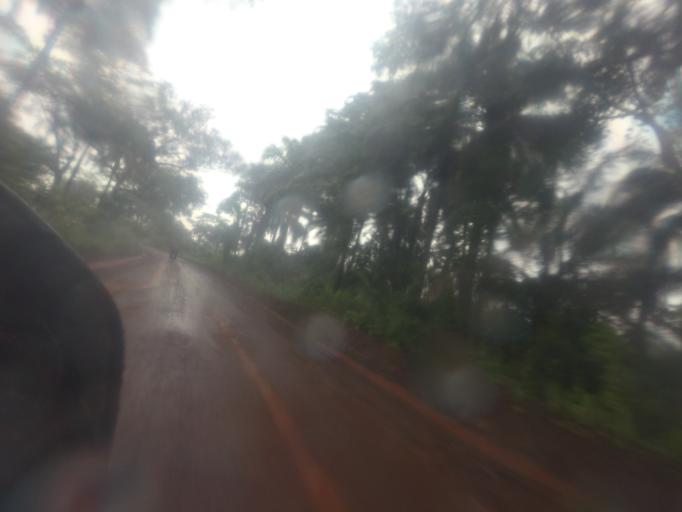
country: SL
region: Northern Province
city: Kambia
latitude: 9.2154
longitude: -12.8556
